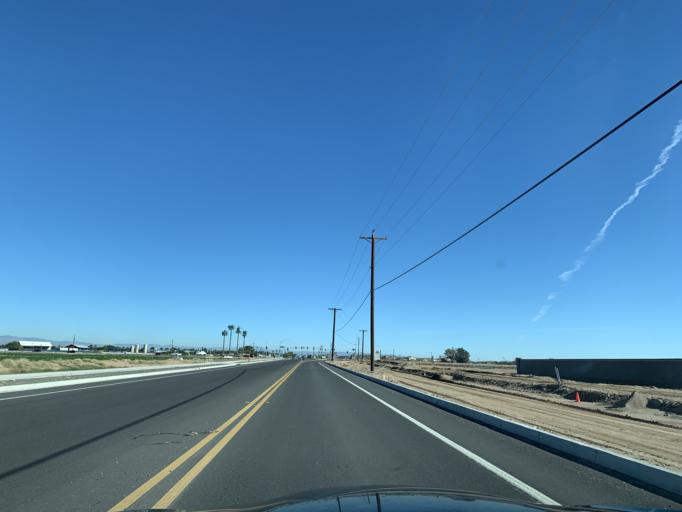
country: US
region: Arizona
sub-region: Maricopa County
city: Queen Creek
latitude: 33.2198
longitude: -111.5894
